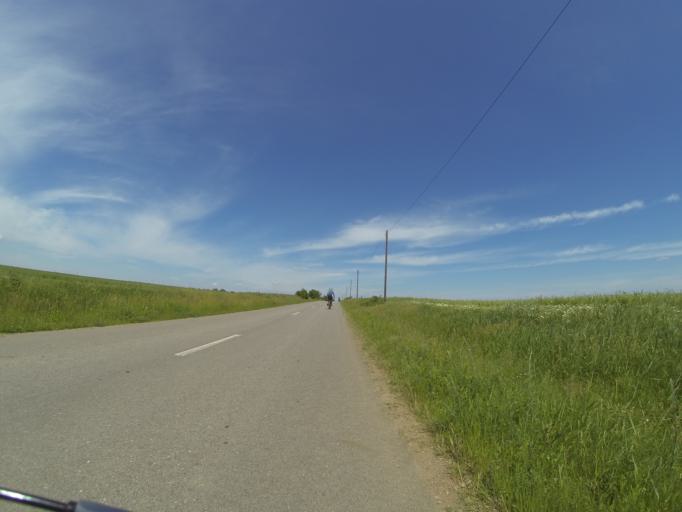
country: RO
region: Dolj
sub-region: Comuna Diosti
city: Radomir
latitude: 44.1489
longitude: 24.1637
